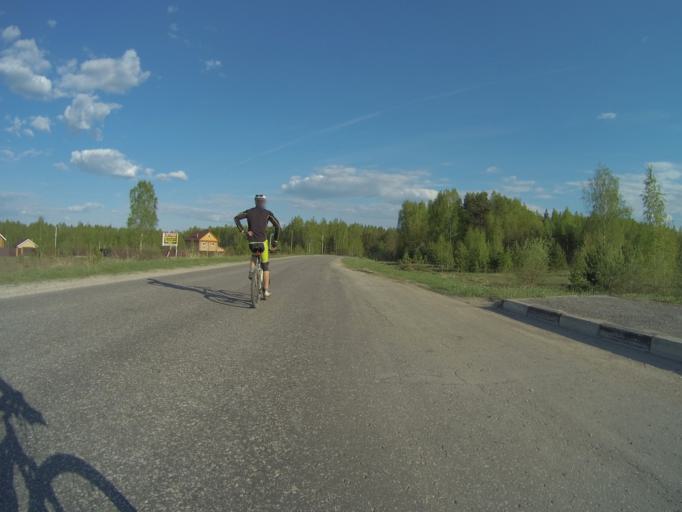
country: RU
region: Vladimir
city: Sudogda
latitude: 56.0980
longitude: 40.7840
